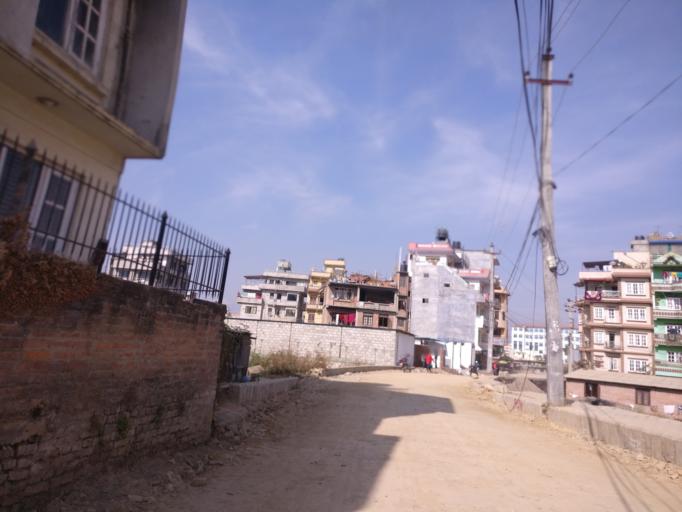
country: NP
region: Central Region
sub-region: Bagmati Zone
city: Patan
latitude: 27.6746
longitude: 85.3321
